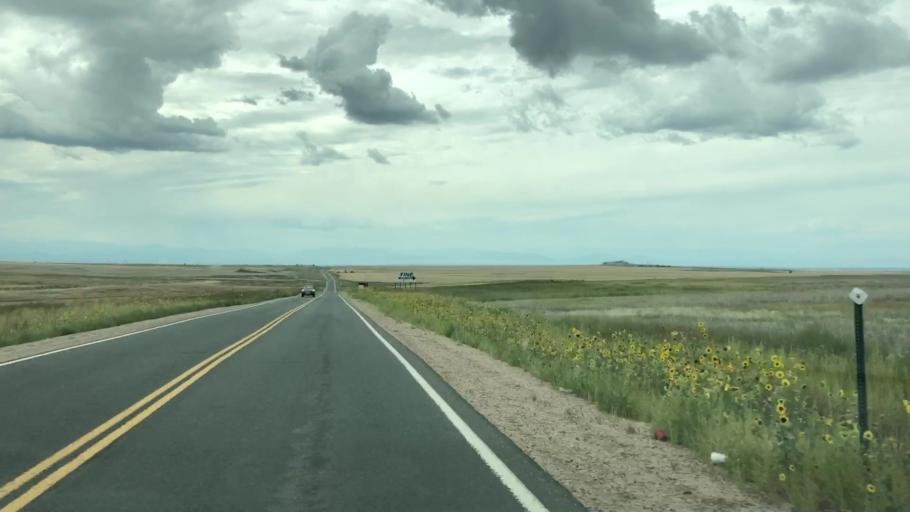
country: US
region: Colorado
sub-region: Adams County
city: Aurora
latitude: 39.7984
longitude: -104.6849
